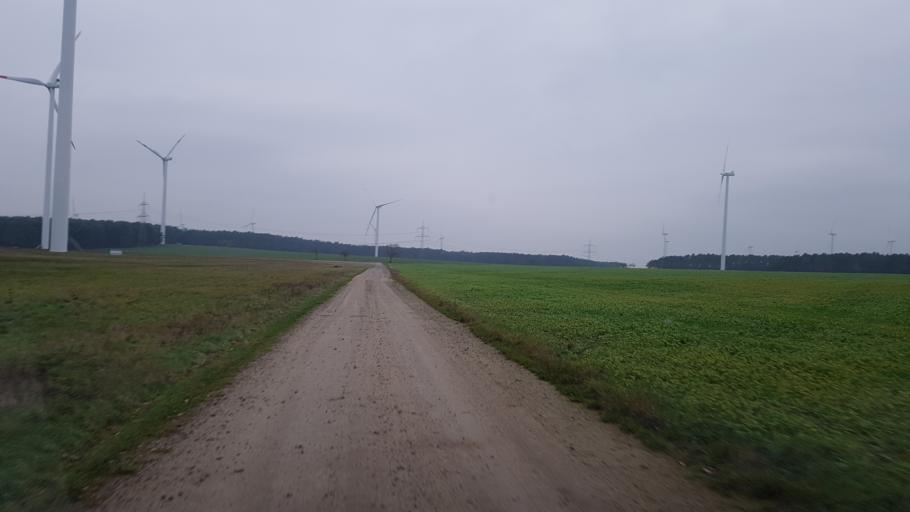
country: DE
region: Brandenburg
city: Schilda
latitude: 51.6523
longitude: 13.3792
